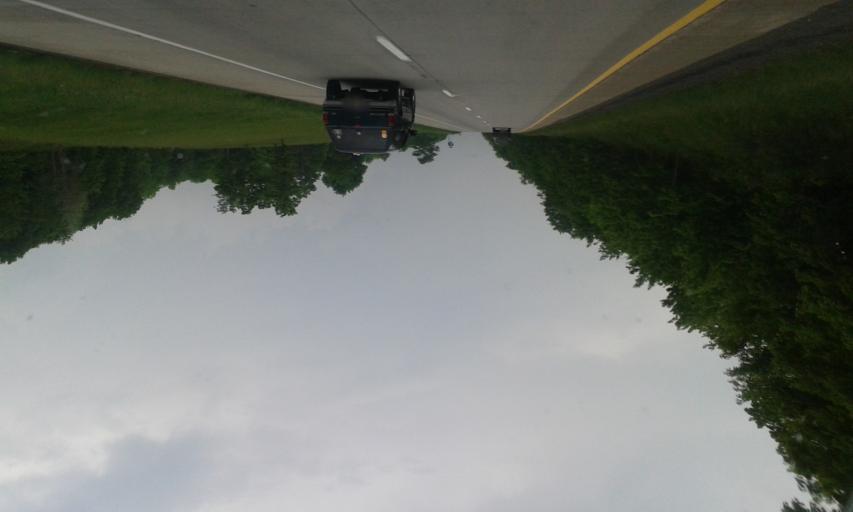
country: US
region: Pennsylvania
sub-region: Lackawanna County
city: Moscow
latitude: 41.2511
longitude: -75.5159
